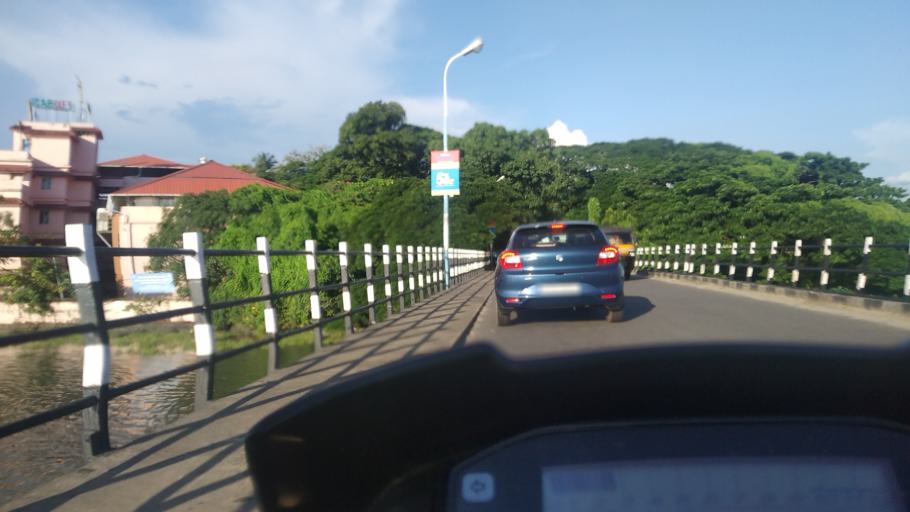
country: IN
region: Kerala
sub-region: Ernakulam
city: Cochin
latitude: 9.9380
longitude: 76.2679
